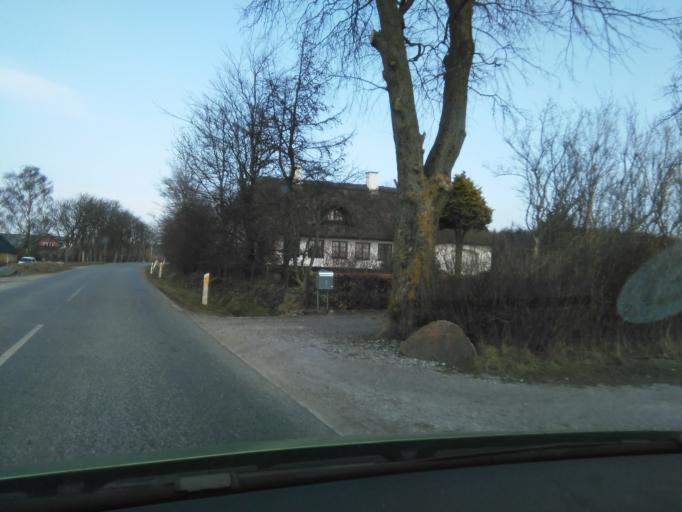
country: DK
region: Central Jutland
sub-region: Arhus Kommune
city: Beder
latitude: 56.0571
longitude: 10.2422
